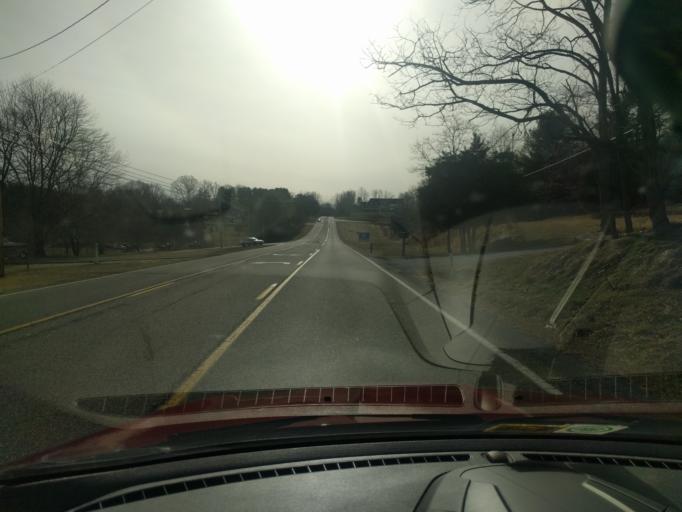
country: US
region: Virginia
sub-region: Augusta County
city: Stuarts Draft
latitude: 37.9956
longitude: -79.1603
